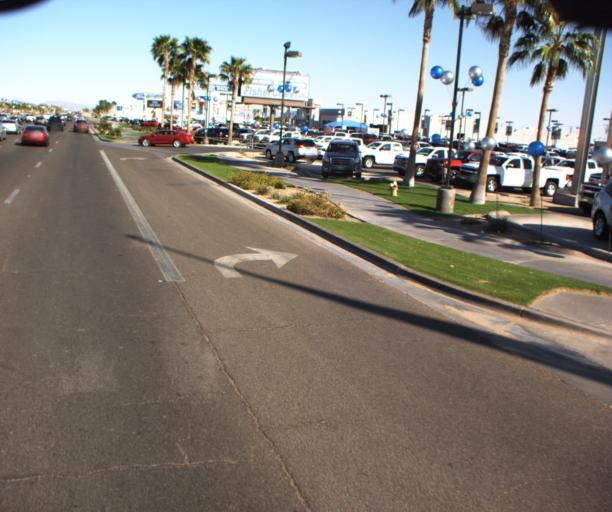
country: US
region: Arizona
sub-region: Yuma County
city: Yuma
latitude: 32.6693
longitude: -114.6130
